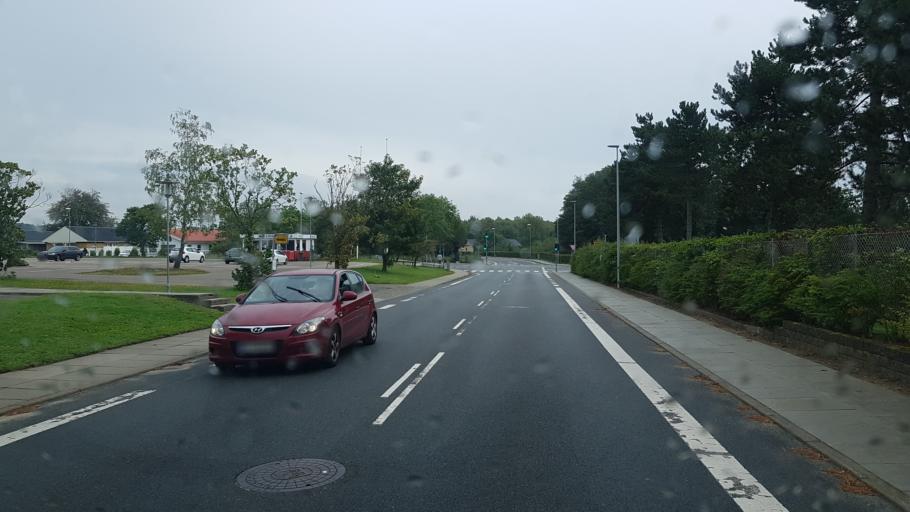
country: DK
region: Central Jutland
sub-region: Silkeborg Kommune
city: Silkeborg
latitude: 56.1830
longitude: 9.5550
